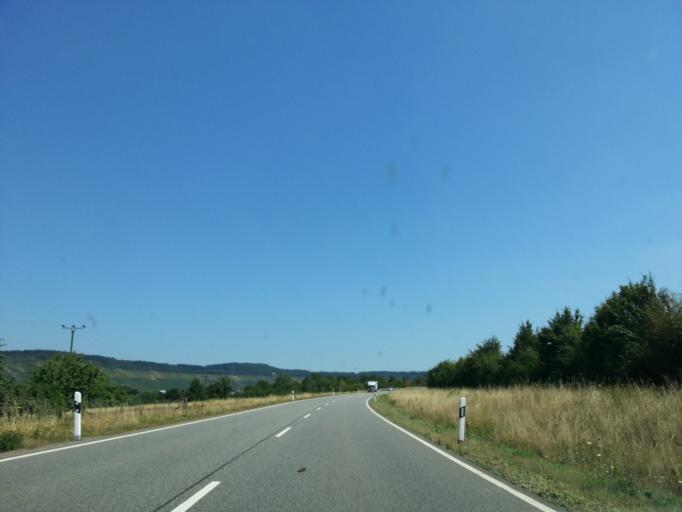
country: DE
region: Rheinland-Pfalz
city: Brauneberg
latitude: 49.9203
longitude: 6.9808
